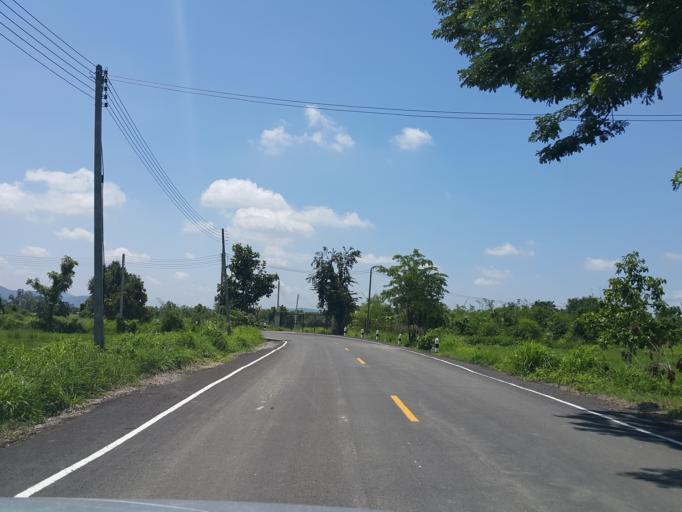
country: TH
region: Lamphun
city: Ban Thi
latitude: 18.6791
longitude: 99.1274
